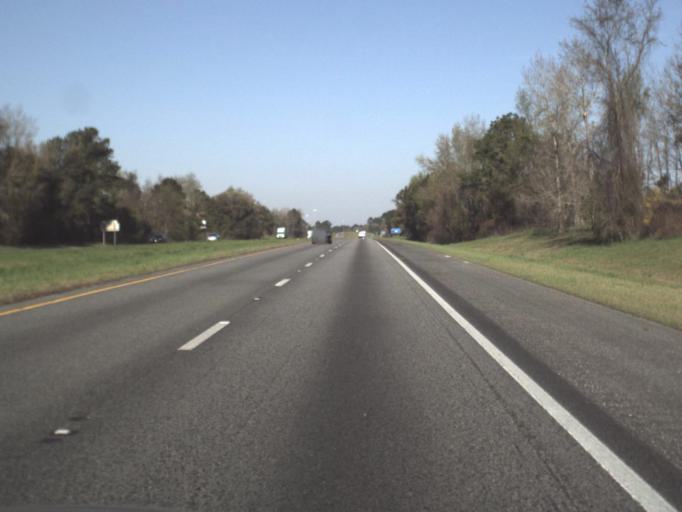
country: US
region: Florida
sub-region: Jefferson County
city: Monticello
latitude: 30.4495
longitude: -83.7494
